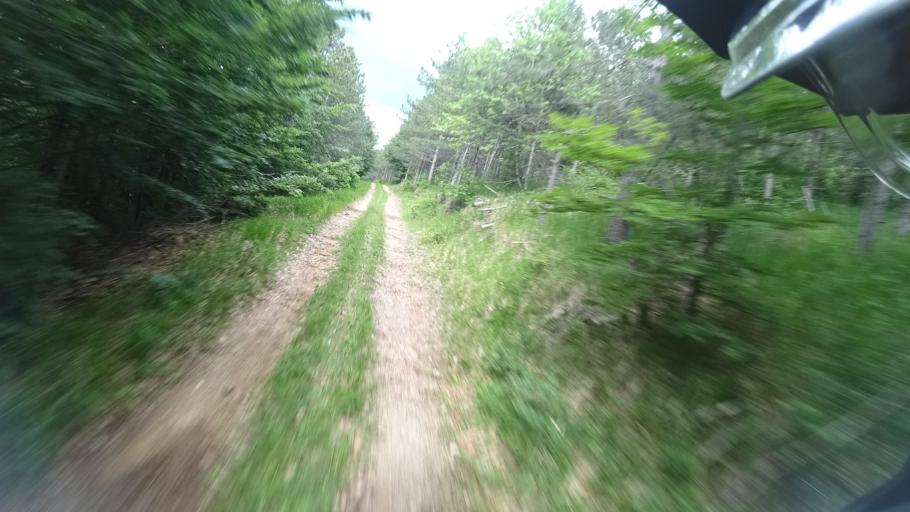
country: HR
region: Zadarska
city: Obrovac
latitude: 44.2725
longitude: 15.7411
